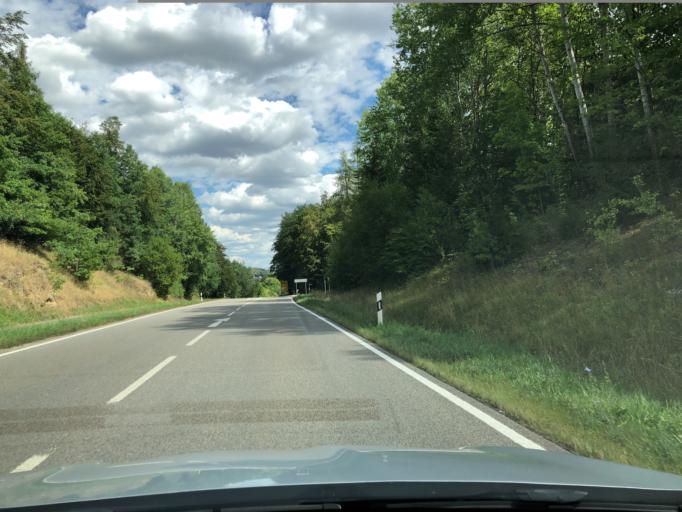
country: DE
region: Bavaria
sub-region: Upper Palatinate
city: Sulzbach-Rosenberg
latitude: 49.4955
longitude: 11.7241
